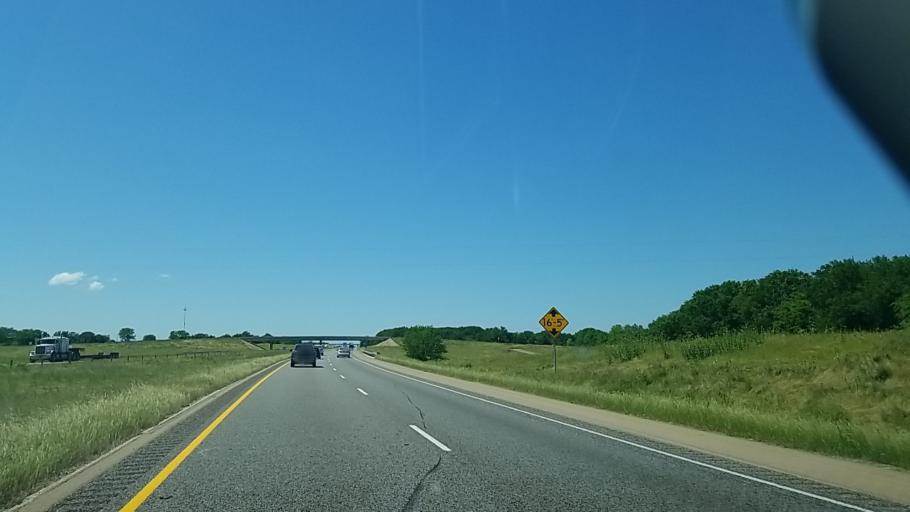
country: US
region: Texas
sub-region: Freestone County
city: Teague
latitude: 31.5825
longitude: -96.1489
